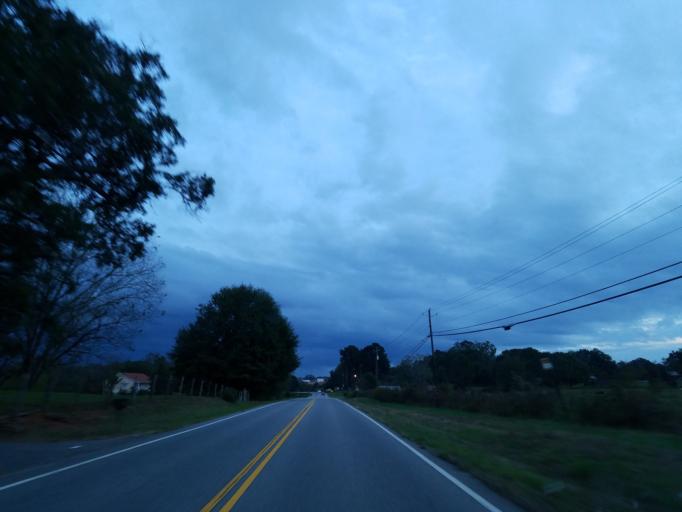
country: US
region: Georgia
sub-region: Forsyth County
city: Cumming
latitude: 34.3117
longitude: -84.1061
